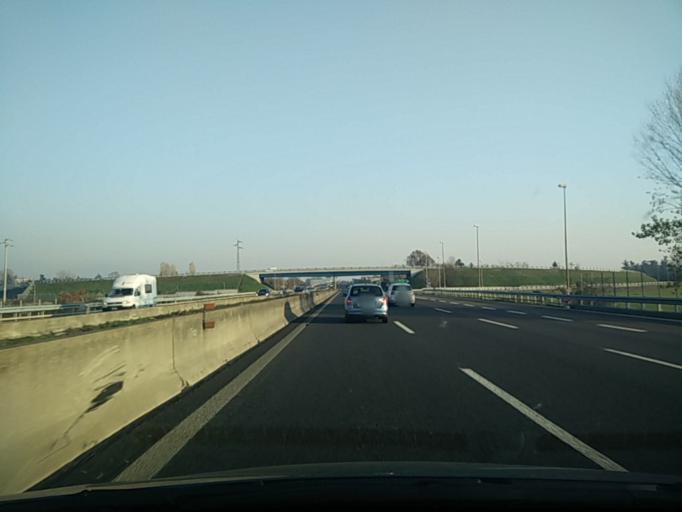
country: IT
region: Lombardy
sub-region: Provincia di Bergamo
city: Telgate
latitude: 45.6336
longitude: 9.8526
